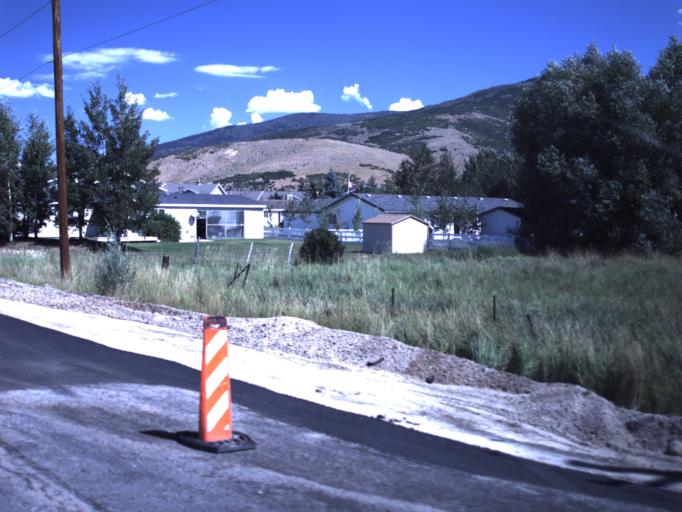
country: US
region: Utah
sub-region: Summit County
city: Kamas
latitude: 40.6323
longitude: -111.2807
